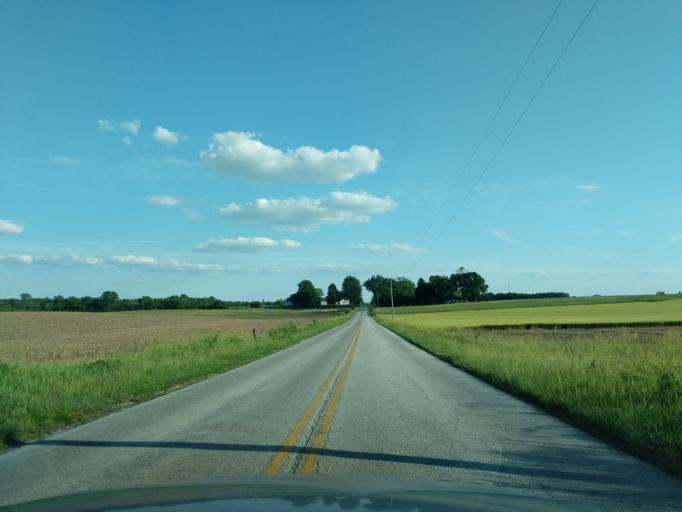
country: US
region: Indiana
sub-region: Huntington County
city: Huntington
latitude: 40.9129
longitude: -85.4714
